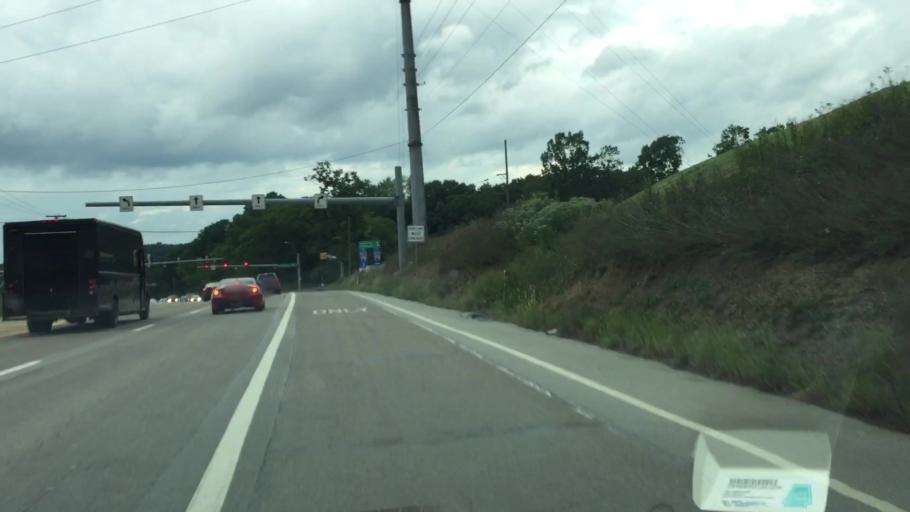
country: US
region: Pennsylvania
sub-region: Butler County
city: Zelienople
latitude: 40.7547
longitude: -80.1169
